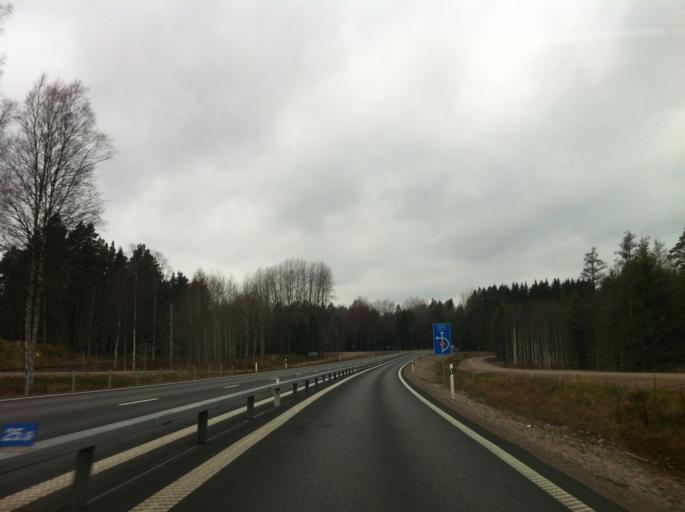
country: SE
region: Joenkoeping
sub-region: Vetlanda Kommun
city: Vetlanda
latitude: 57.4240
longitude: 15.1329
